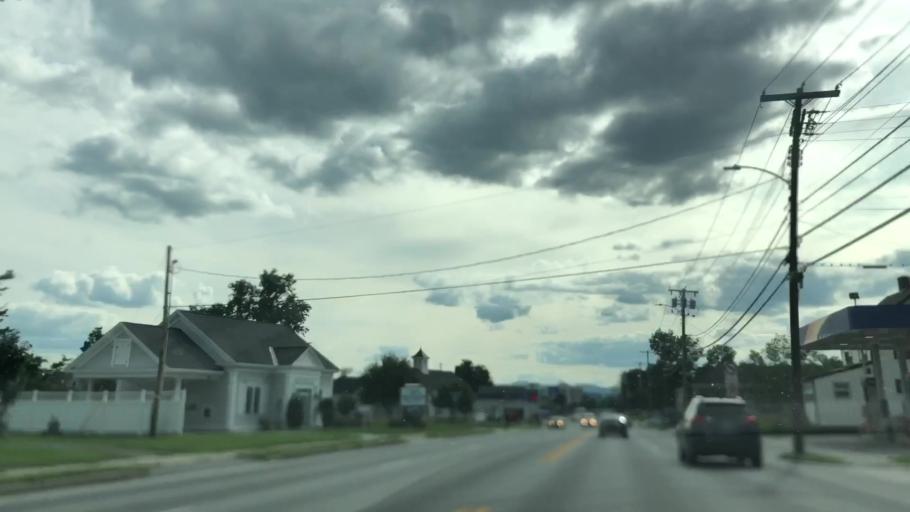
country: US
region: Vermont
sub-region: Rutland County
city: Rutland
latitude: 43.6140
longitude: -72.9635
